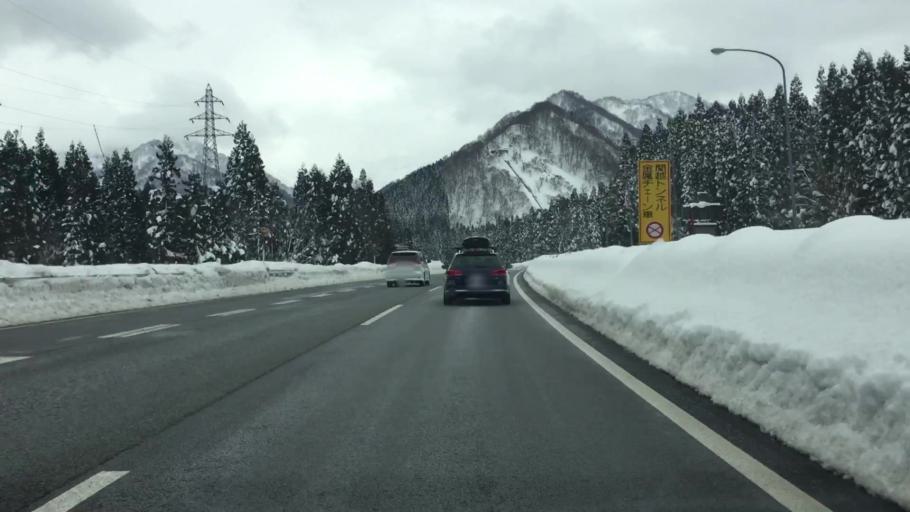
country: JP
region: Niigata
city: Shiozawa
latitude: 36.8845
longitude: 138.8517
